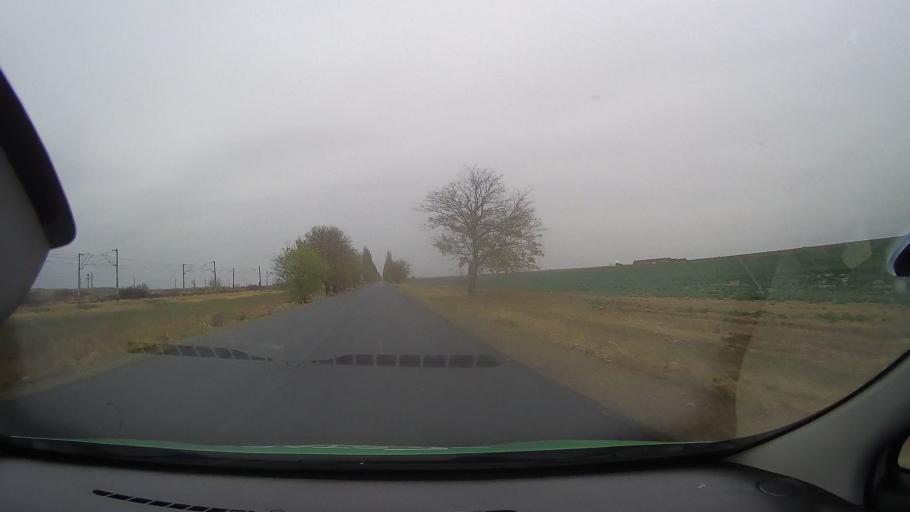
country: RO
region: Ialomita
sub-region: Comuna Valea Ciorii
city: Valea Ciorii
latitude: 44.7068
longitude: 27.5943
